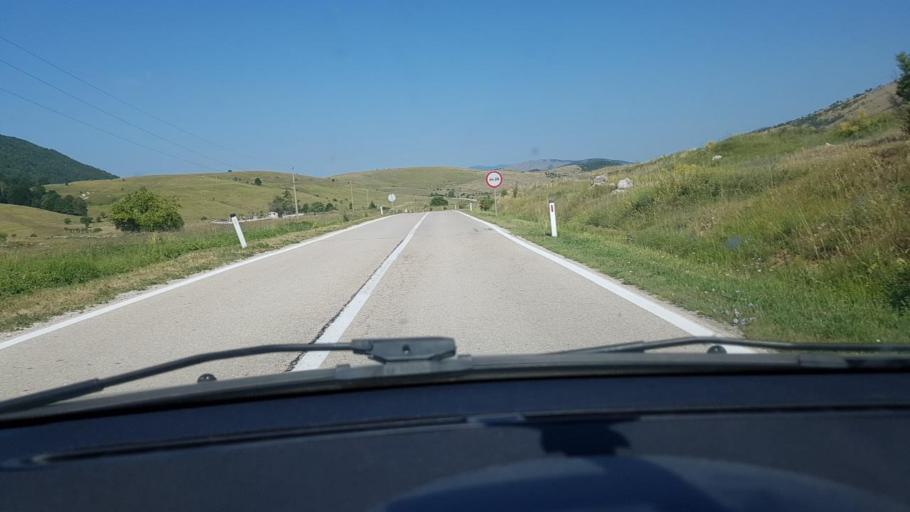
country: BA
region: Federation of Bosnia and Herzegovina
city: Bosansko Grahovo
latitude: 44.1259
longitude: 16.5211
